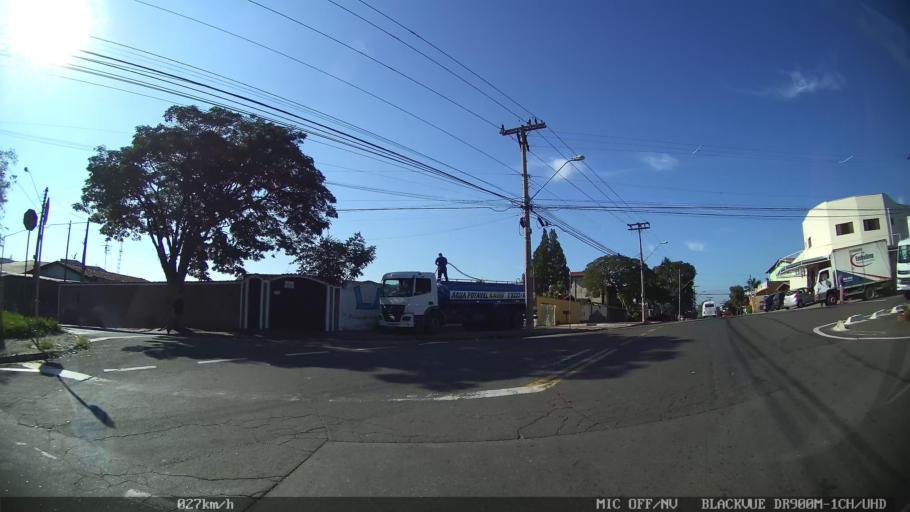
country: BR
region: Sao Paulo
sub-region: Campinas
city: Campinas
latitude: -22.9645
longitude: -47.1078
